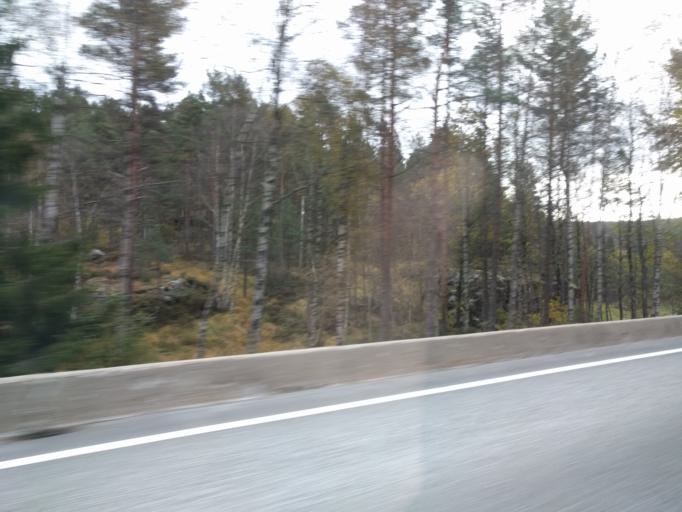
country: NO
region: Aust-Agder
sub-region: Iveland
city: Birketveit
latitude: 58.3581
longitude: 7.8004
